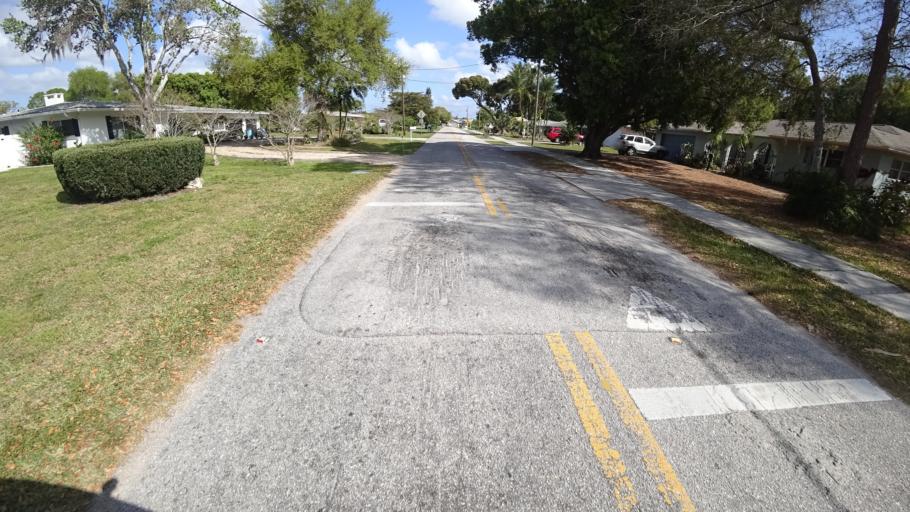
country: US
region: Florida
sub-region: Manatee County
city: Whitfield
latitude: 27.4234
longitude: -82.5596
